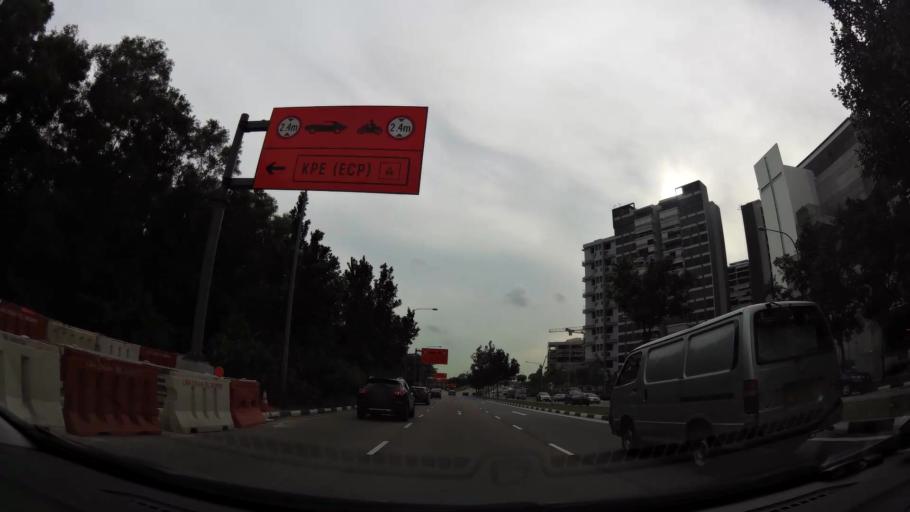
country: MY
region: Johor
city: Kampung Pasir Gudang Baru
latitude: 1.3915
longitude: 103.9141
